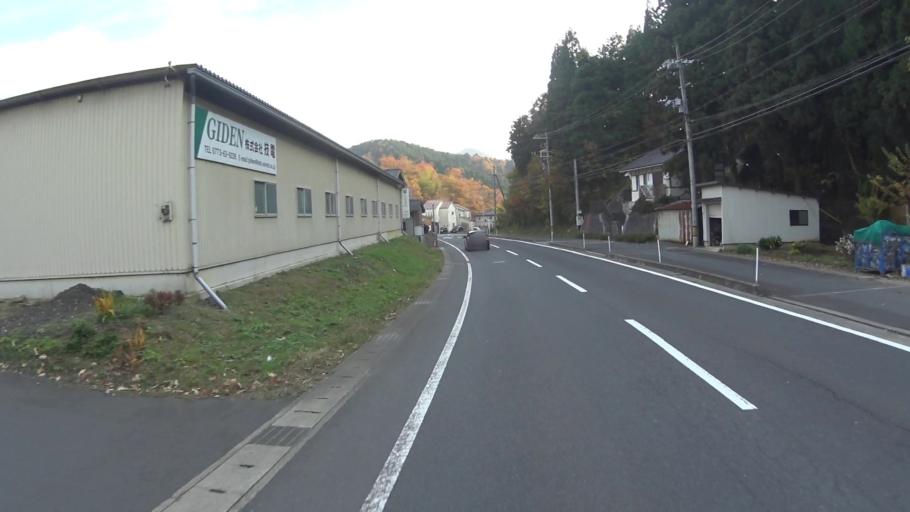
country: JP
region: Kyoto
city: Maizuru
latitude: 35.4913
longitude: 135.4365
